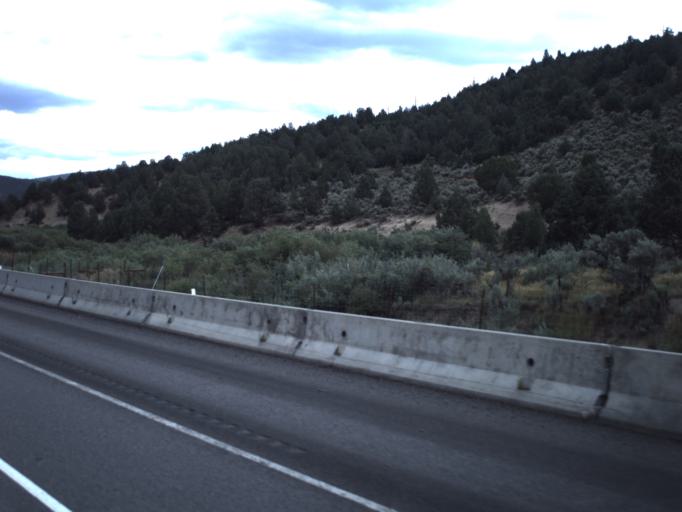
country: US
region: Utah
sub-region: Utah County
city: Mapleton
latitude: 39.9546
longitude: -111.2329
